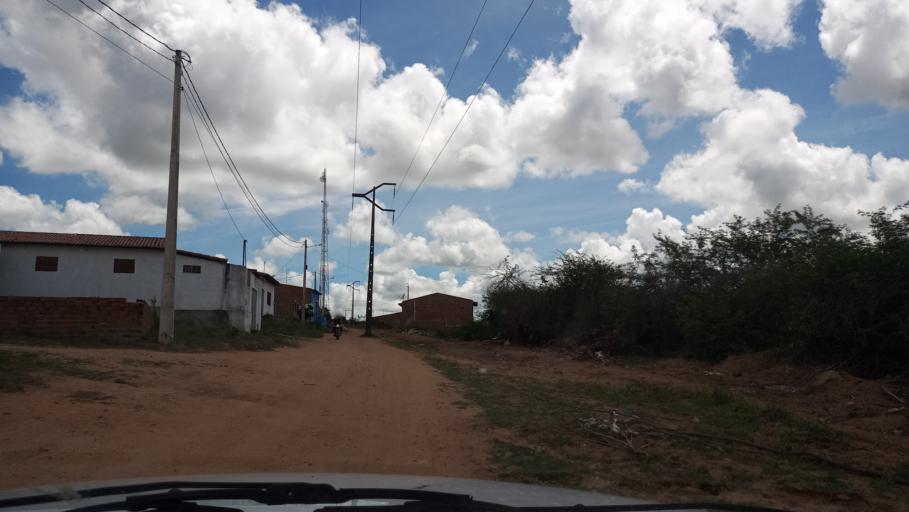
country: BR
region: Rio Grande do Norte
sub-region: Sao Paulo Do Potengi
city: Sao Paulo do Potengi
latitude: -5.9015
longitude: -35.7710
